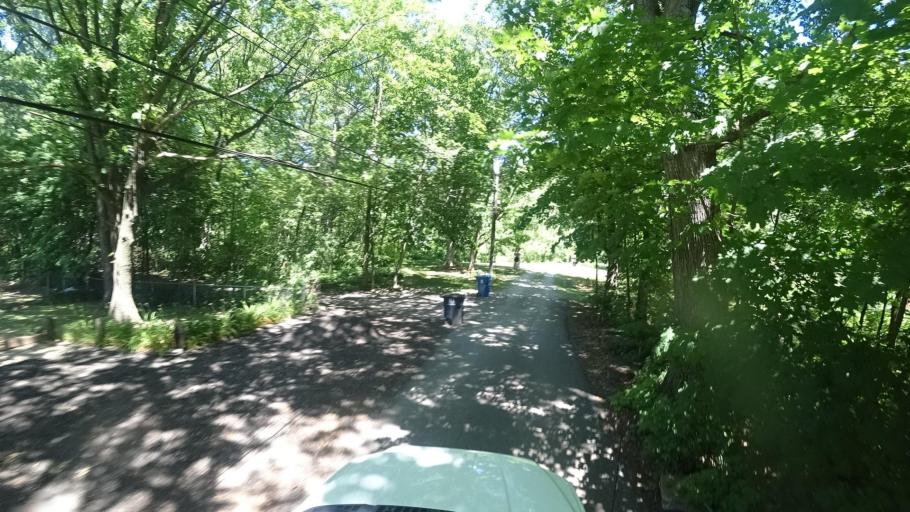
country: US
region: Indiana
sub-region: Porter County
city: Porter
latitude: 41.6360
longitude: -87.0741
